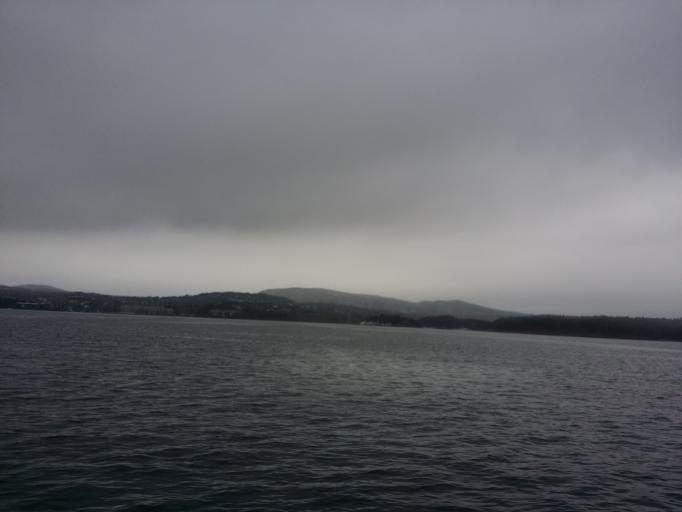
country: NO
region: Akershus
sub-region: Baerum
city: Lysaker
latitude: 59.8929
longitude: 10.6533
